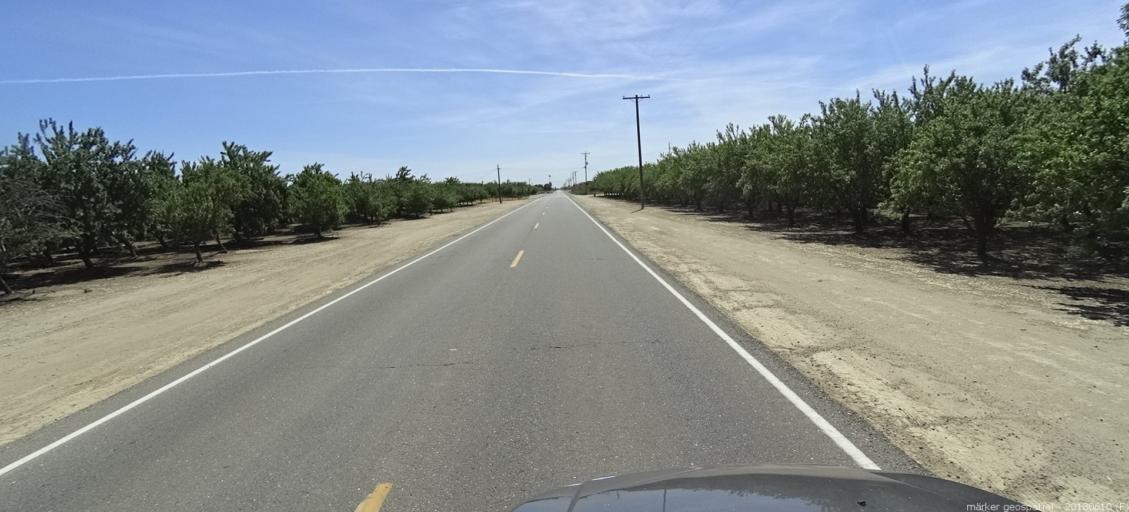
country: US
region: California
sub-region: Madera County
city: Chowchilla
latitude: 37.0182
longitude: -120.3033
